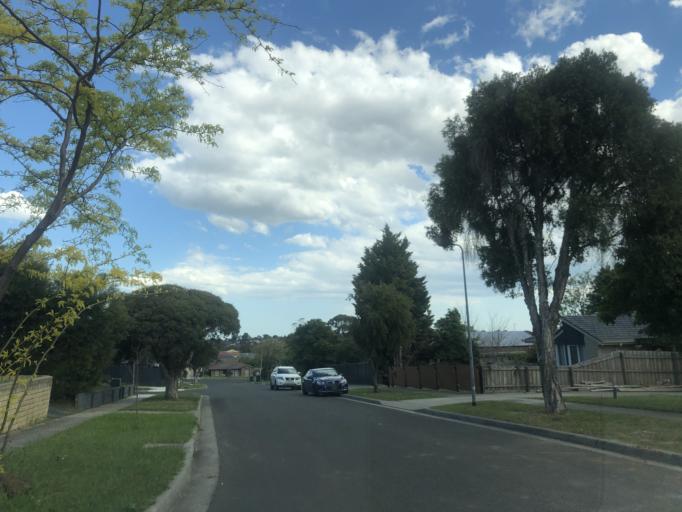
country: AU
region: Victoria
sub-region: Casey
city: Endeavour Hills
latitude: -37.9885
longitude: 145.2618
